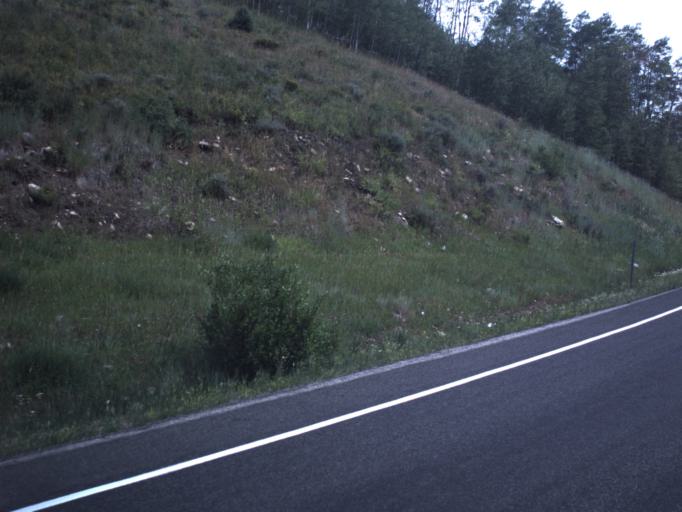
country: US
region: Utah
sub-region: Summit County
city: Francis
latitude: 40.5154
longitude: -111.0668
